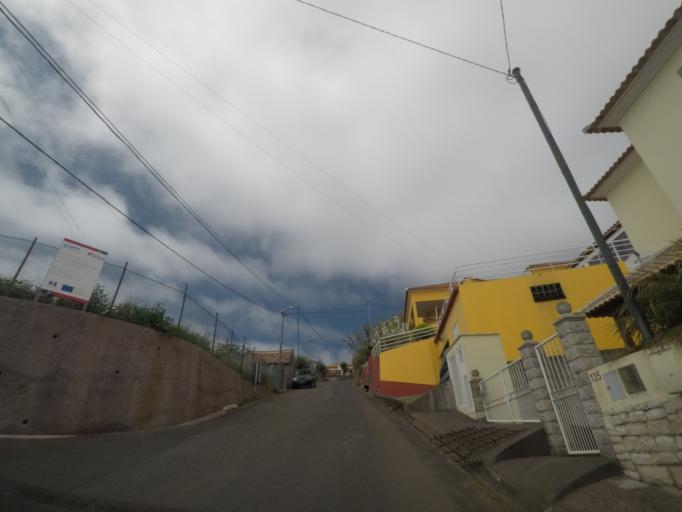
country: PT
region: Madeira
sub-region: Calheta
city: Arco da Calheta
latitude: 32.7159
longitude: -17.1249
